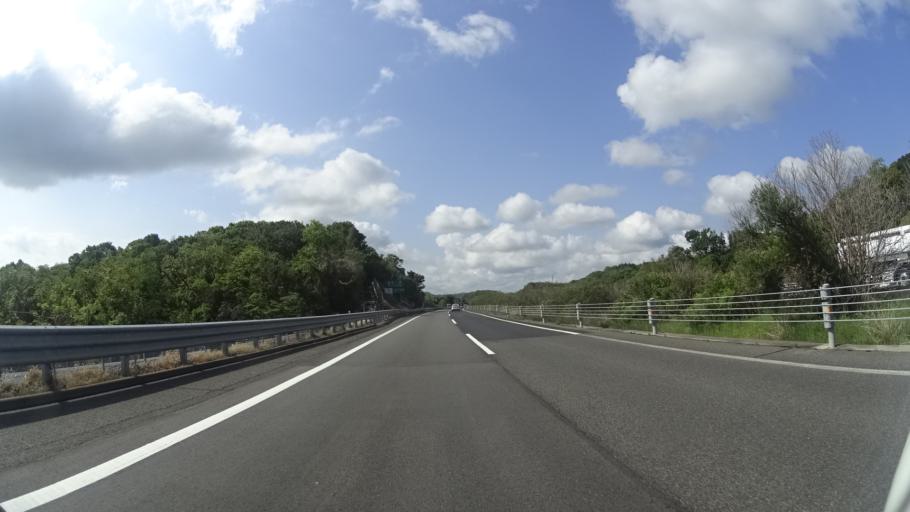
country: JP
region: Hyogo
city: Sumoto
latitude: 34.4547
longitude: 134.8781
